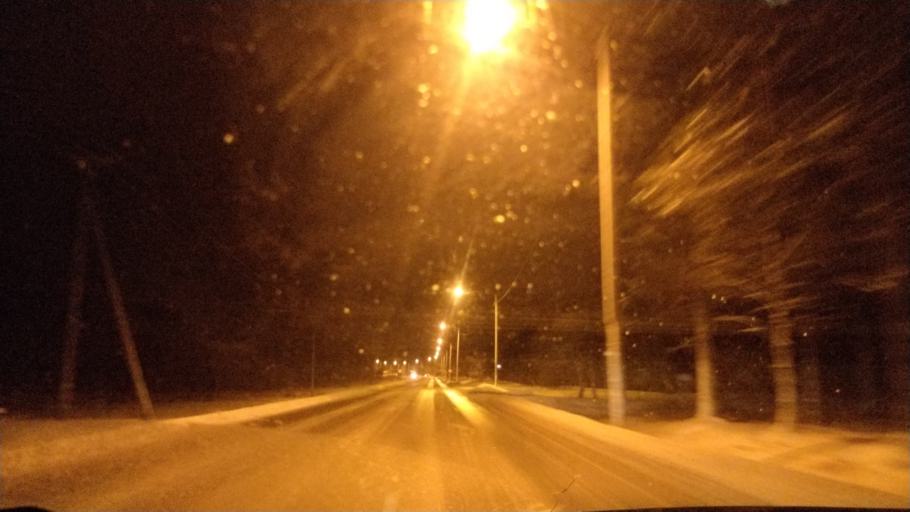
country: FI
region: Lapland
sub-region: Rovaniemi
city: Rovaniemi
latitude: 66.3051
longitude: 25.3572
